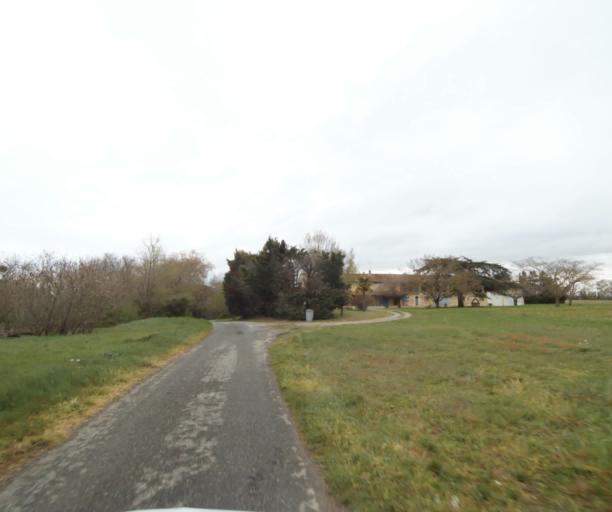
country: FR
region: Midi-Pyrenees
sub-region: Departement de l'Ariege
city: Saverdun
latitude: 43.2159
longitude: 1.5997
